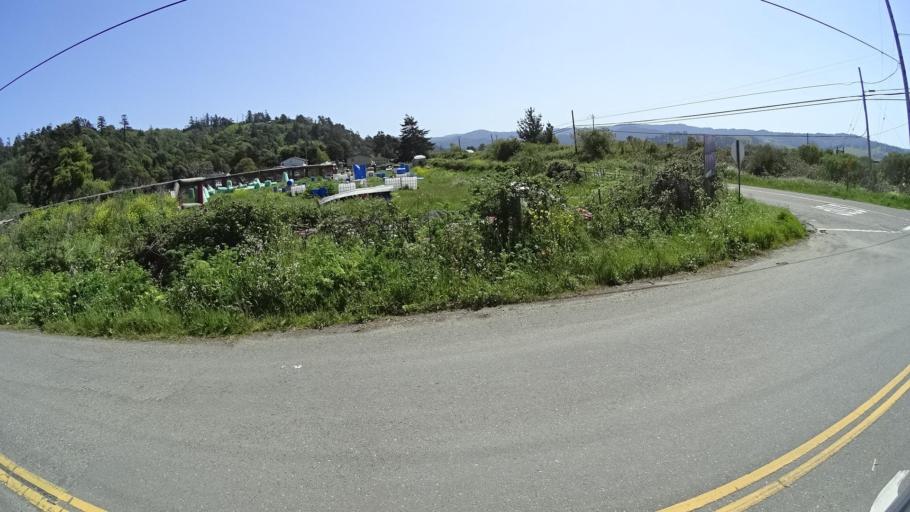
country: US
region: California
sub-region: Humboldt County
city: Fortuna
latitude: 40.5630
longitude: -124.1465
